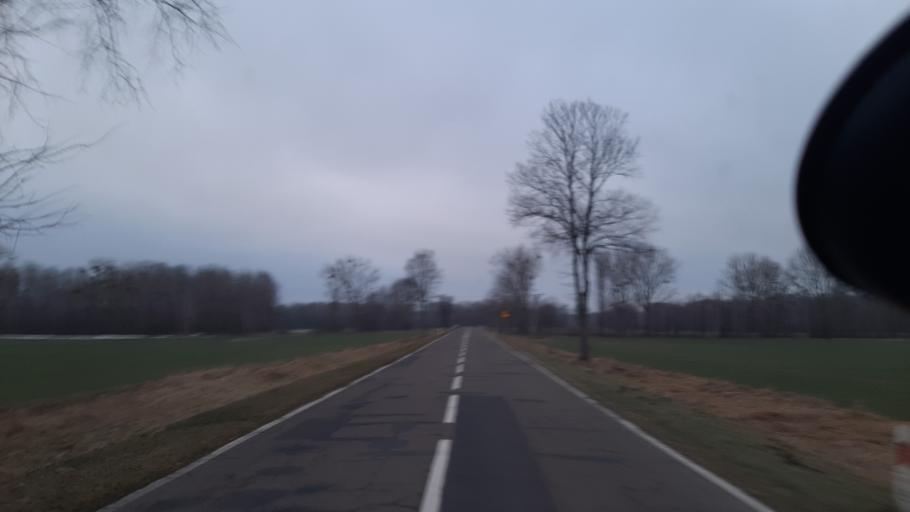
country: PL
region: Lublin Voivodeship
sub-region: Powiat parczewski
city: Sosnowica
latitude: 51.5969
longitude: 23.1533
